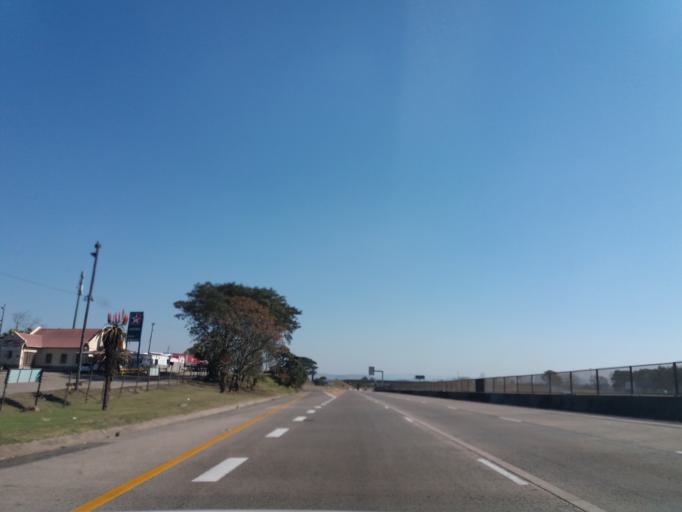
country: ZA
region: KwaZulu-Natal
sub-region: uMgungundlovu District Municipality
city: Camperdown
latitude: -29.7334
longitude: 30.5874
